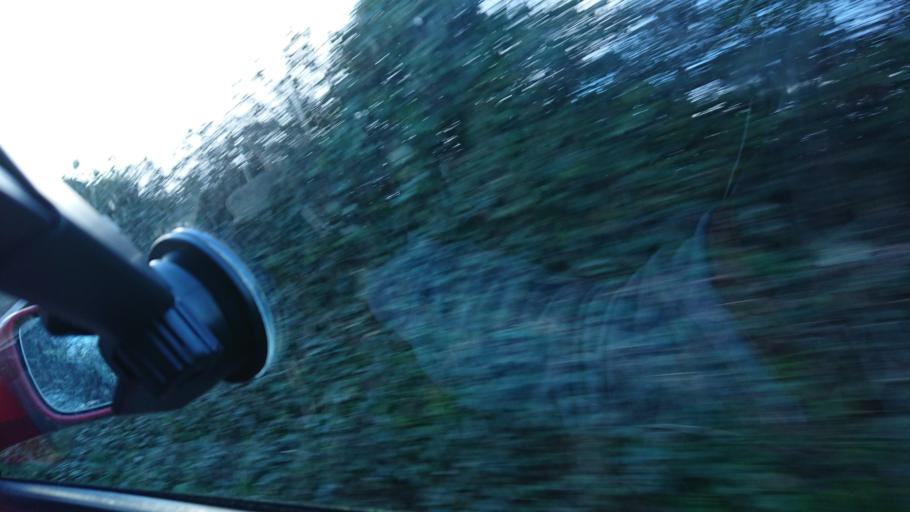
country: GB
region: England
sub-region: Cornwall
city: Looe
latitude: 50.3421
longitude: -4.4804
